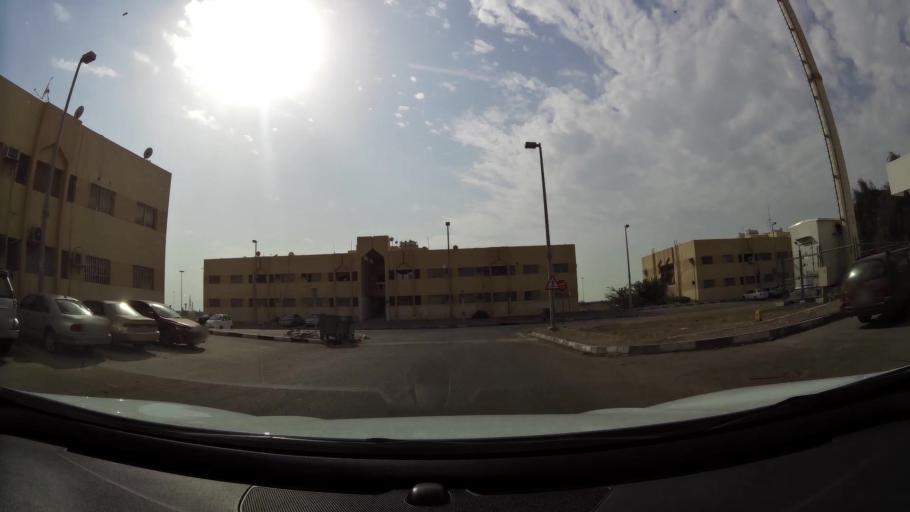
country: AE
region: Abu Dhabi
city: Abu Dhabi
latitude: 24.3178
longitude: 54.5314
